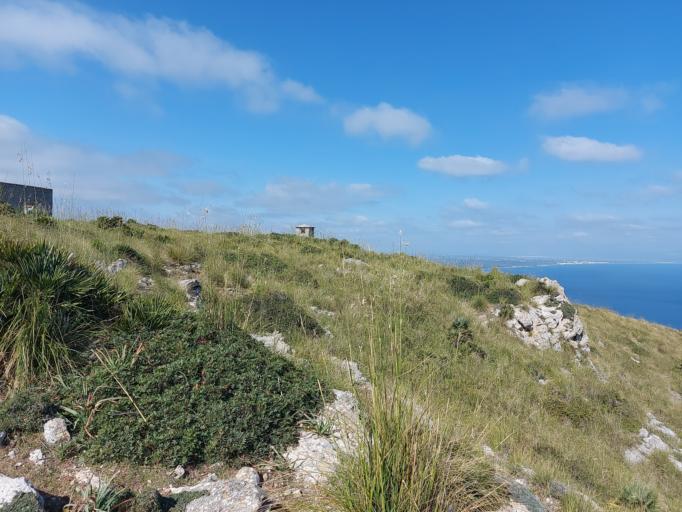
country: ES
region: Balearic Islands
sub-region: Illes Balears
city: Arta
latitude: 39.7385
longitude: 3.3080
